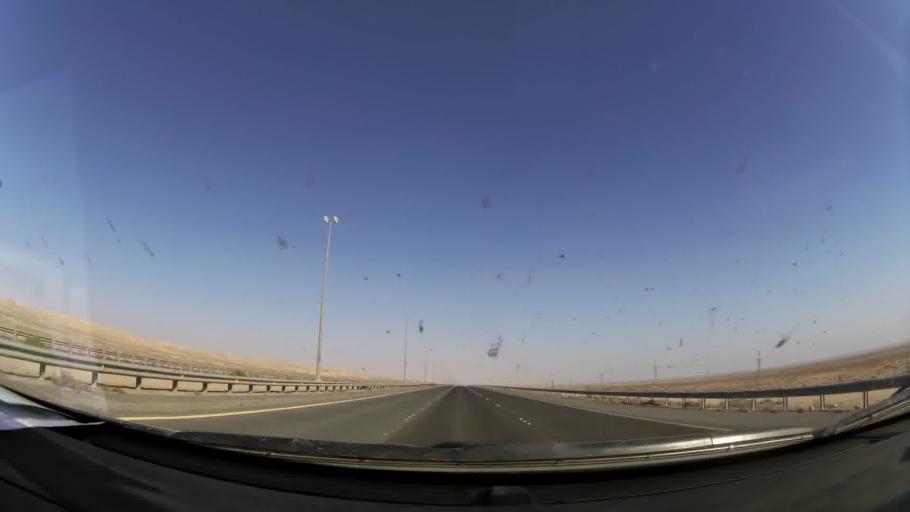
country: KW
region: Al Asimah
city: Kuwait City
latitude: 29.5350
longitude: 47.8379
